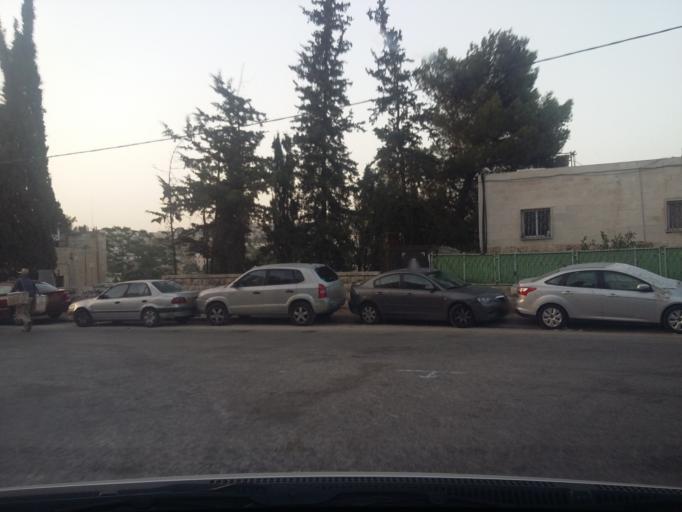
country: PS
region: West Bank
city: East Jerusalem
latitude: 31.7872
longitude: 35.2365
